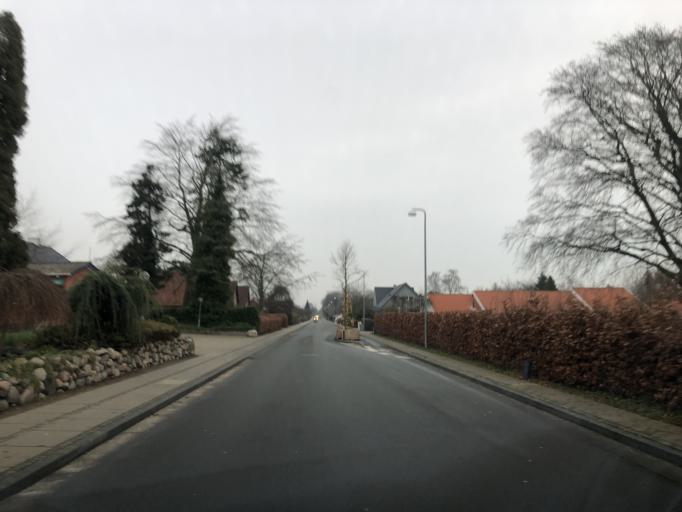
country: DK
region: South Denmark
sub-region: Faaborg-Midtfyn Kommune
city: Arslev
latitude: 55.3029
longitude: 10.4750
